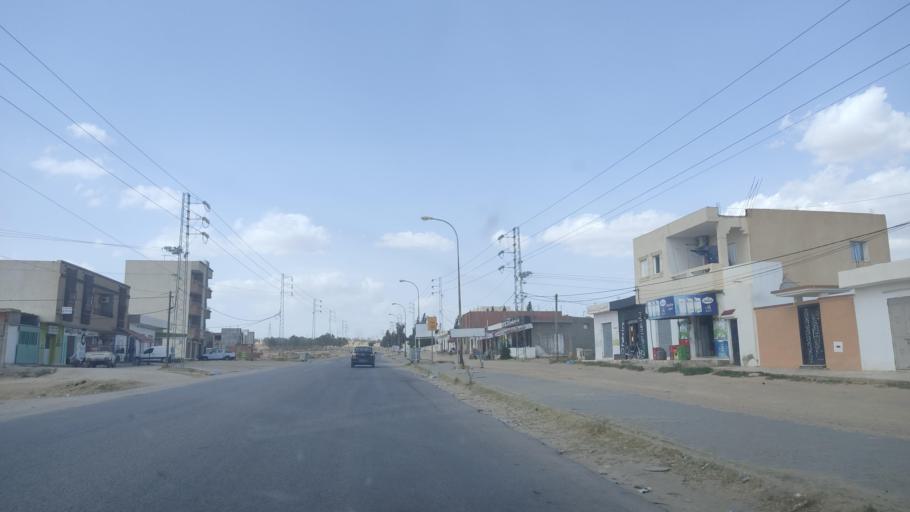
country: TN
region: Sidi Bu Zayd
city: Sidi Bouzid
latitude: 35.1024
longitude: 9.5349
